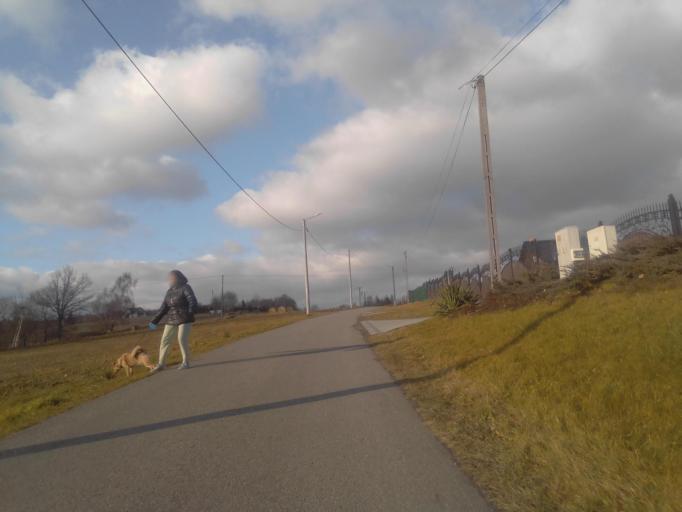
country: PL
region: Subcarpathian Voivodeship
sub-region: Powiat strzyzowski
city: Babica
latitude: 49.9384
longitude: 21.8973
